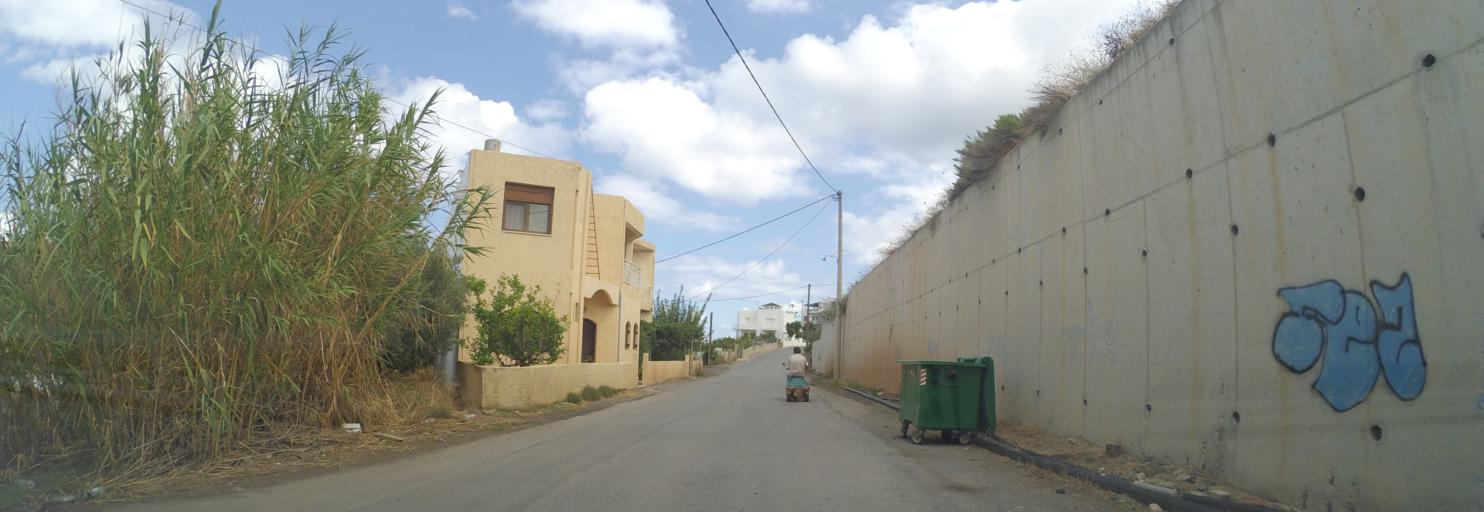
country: GR
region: Crete
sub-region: Nomos Irakleiou
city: Kokkini Hani
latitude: 35.3283
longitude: 25.2632
